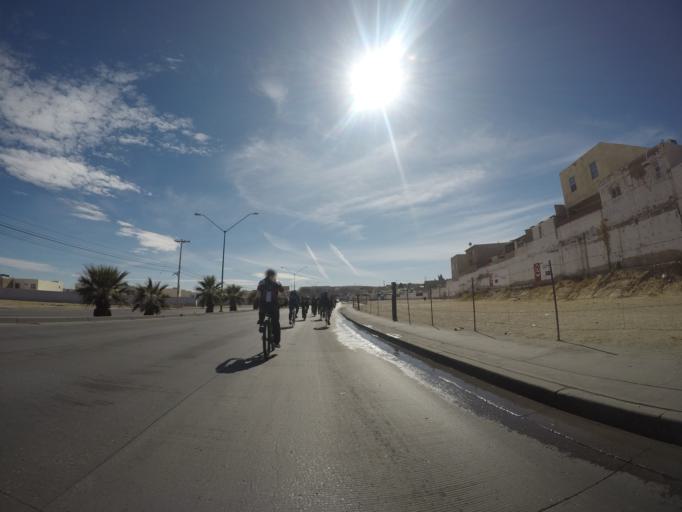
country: MX
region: Chihuahua
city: Ciudad Juarez
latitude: 31.6741
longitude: -106.4054
